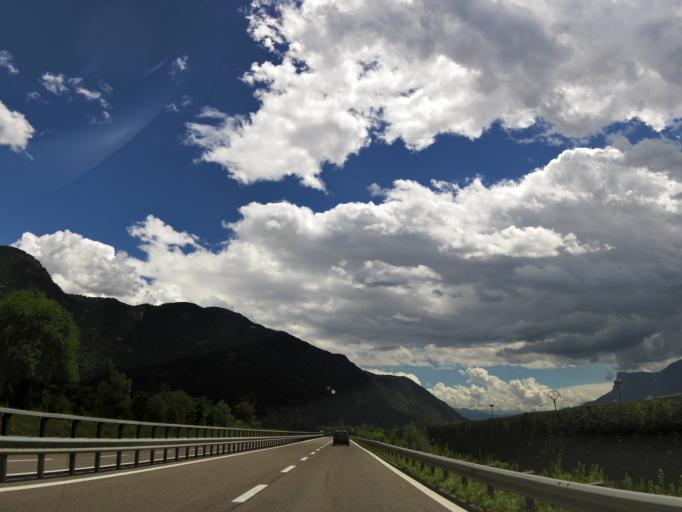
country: IT
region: Trentino-Alto Adige
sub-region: Bolzano
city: Marlengo
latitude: 46.6462
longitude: 11.1597
